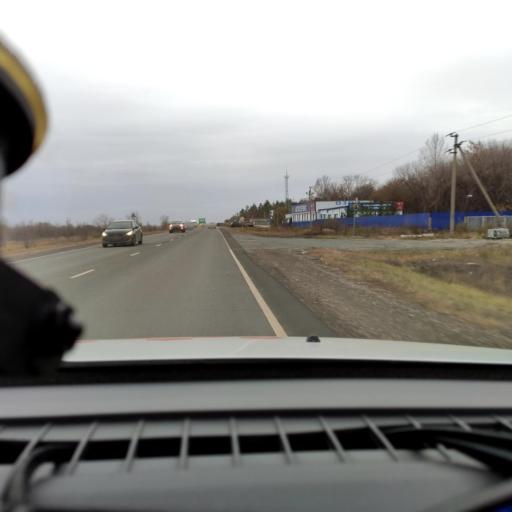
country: RU
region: Samara
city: Samara
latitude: 53.1239
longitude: 50.1887
